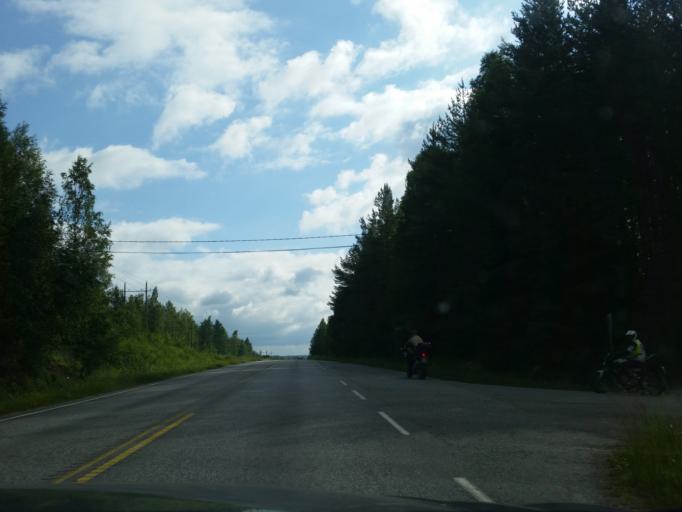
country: FI
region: Northern Savo
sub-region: Kuopio
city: Karttula
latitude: 62.9016
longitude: 26.9449
